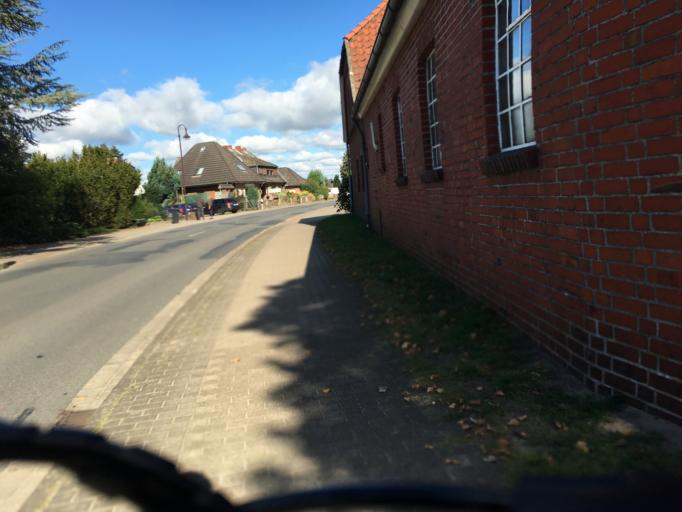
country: DE
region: Lower Saxony
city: Bardowick
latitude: 53.3018
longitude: 10.3867
